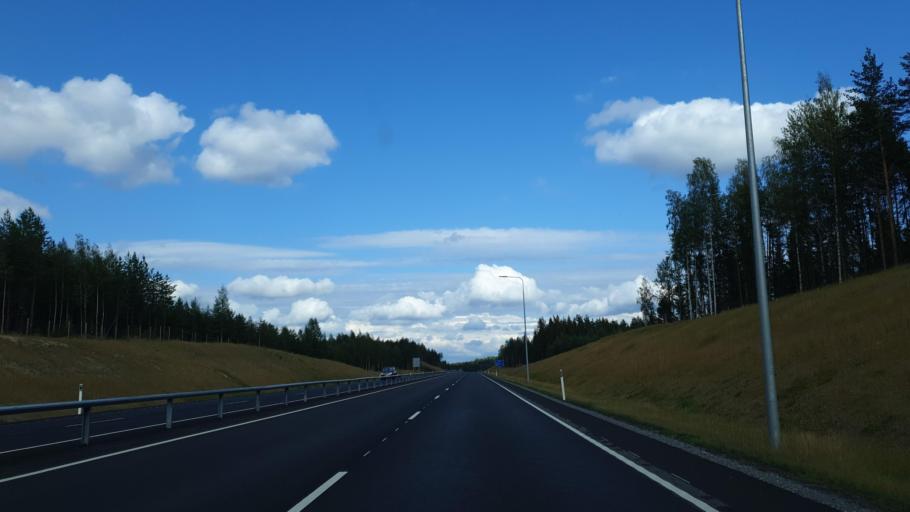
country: FI
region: Southern Savonia
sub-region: Mikkeli
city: Mikkeli
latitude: 61.7383
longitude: 27.4317
